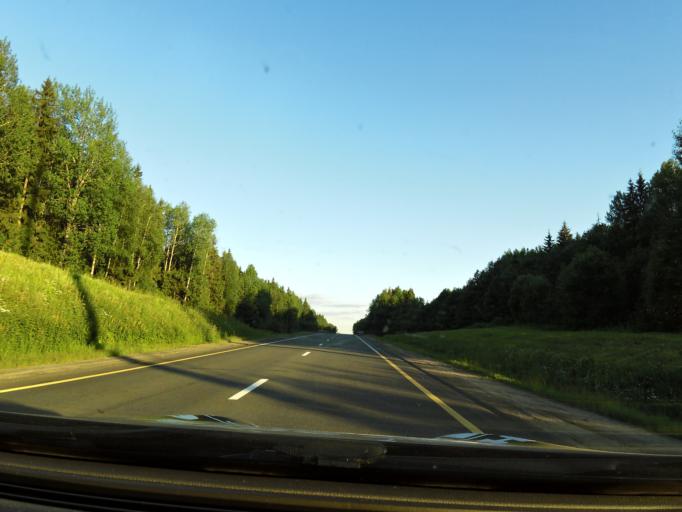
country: RU
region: Vologda
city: Gryazovets
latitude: 58.6932
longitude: 40.3012
